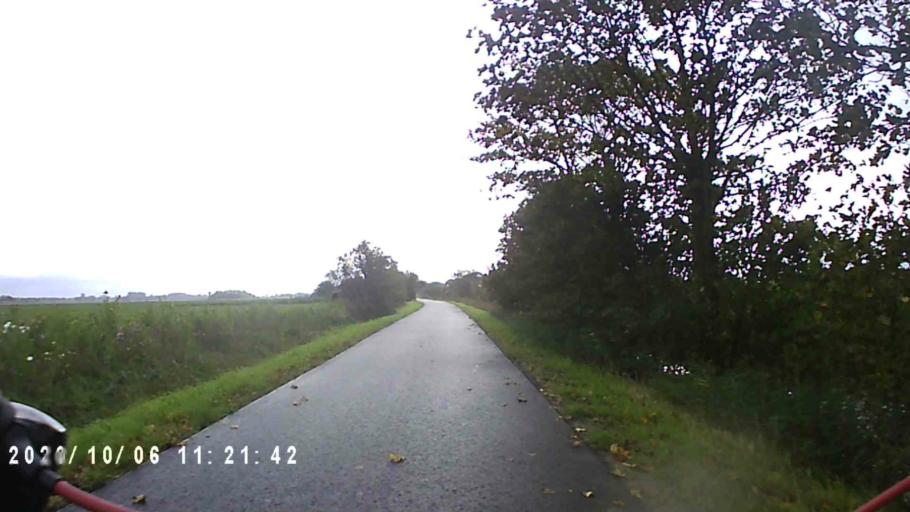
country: NL
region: Groningen
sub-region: Gemeente Zuidhorn
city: Oldehove
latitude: 53.3468
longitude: 6.4085
